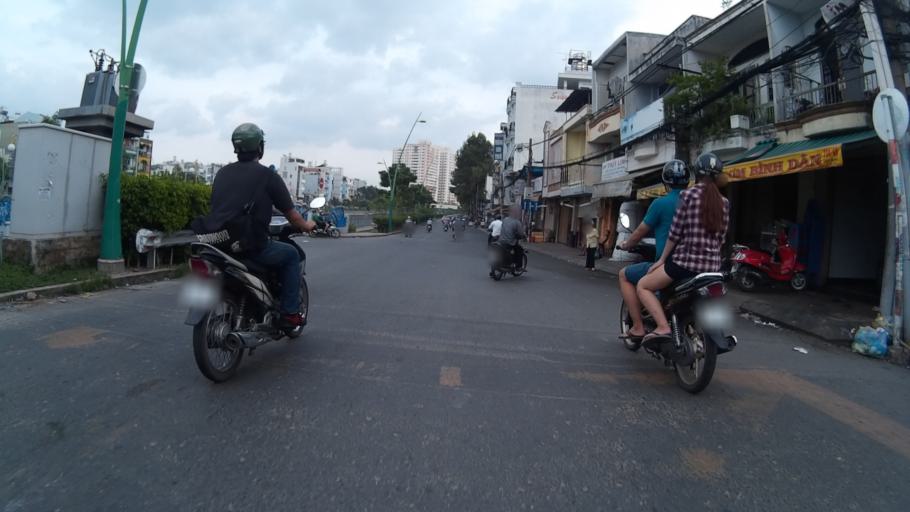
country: VN
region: Ho Chi Minh City
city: Quan Phu Nhuan
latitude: 10.7877
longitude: 106.6707
